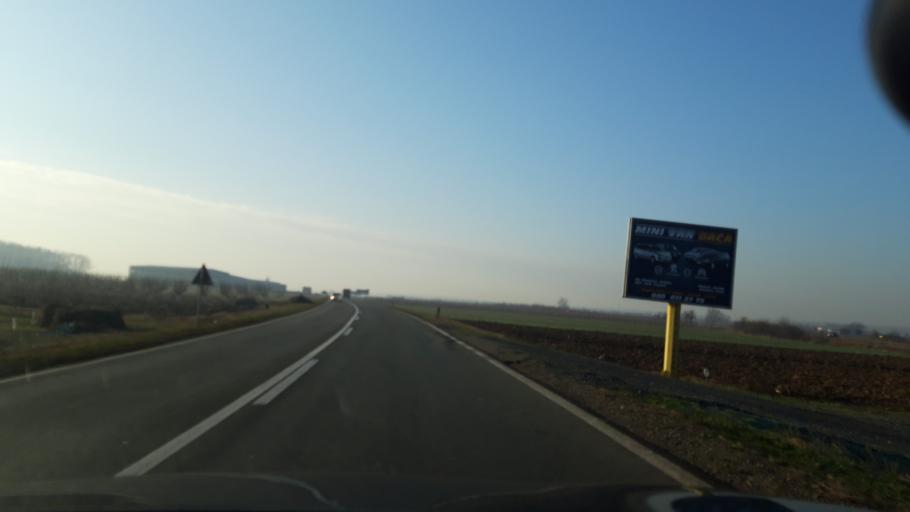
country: RS
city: Klenak
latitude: 44.8011
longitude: 19.7308
